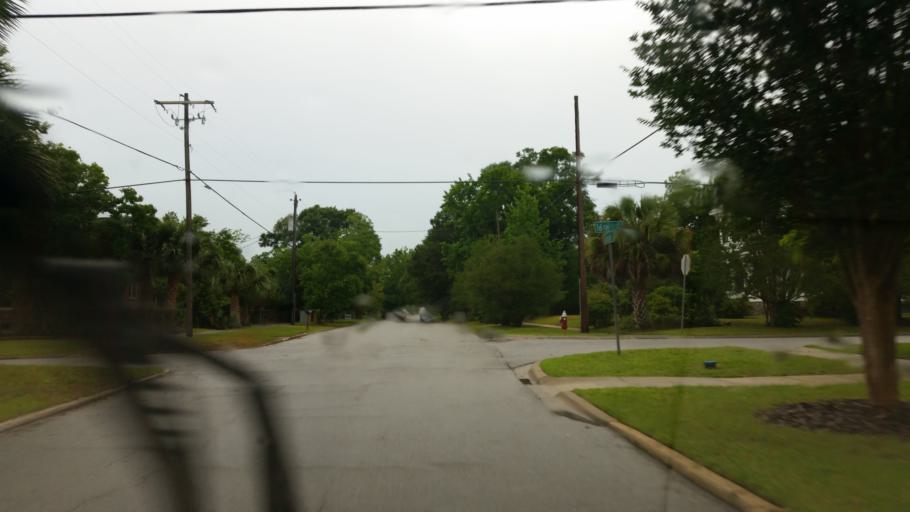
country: US
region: Florida
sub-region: Escambia County
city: East Pensacola Heights
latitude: 30.4230
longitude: -87.1960
